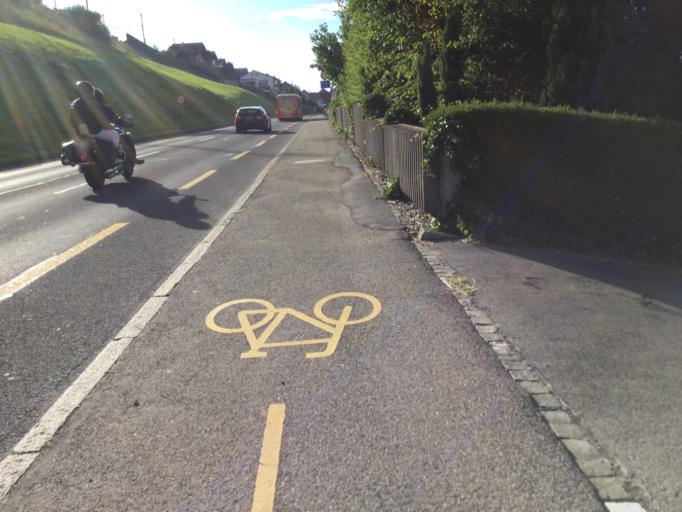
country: CH
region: Bern
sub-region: Thun District
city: Hilterfingen
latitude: 46.7086
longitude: 7.6464
